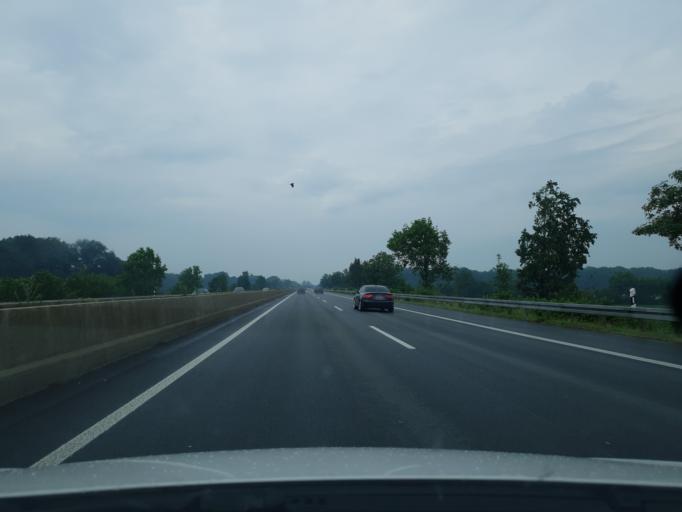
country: DE
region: North Rhine-Westphalia
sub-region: Regierungsbezirk Munster
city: Legden
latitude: 52.0389
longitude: 7.0617
